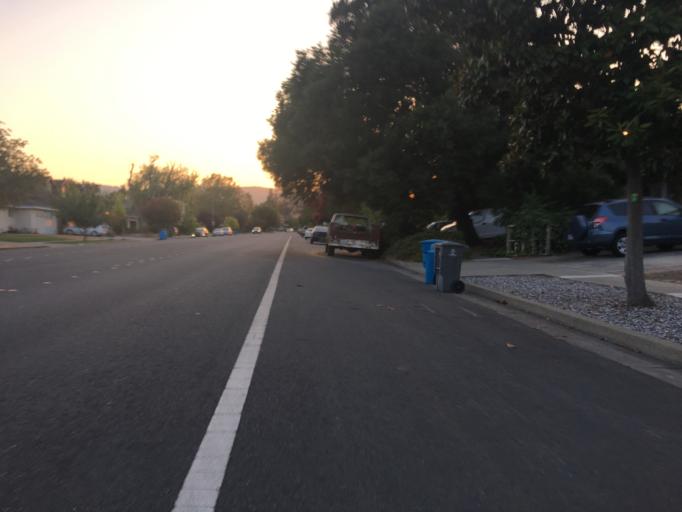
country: US
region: California
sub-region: Santa Clara County
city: Cupertino
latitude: 37.3124
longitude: -122.0351
